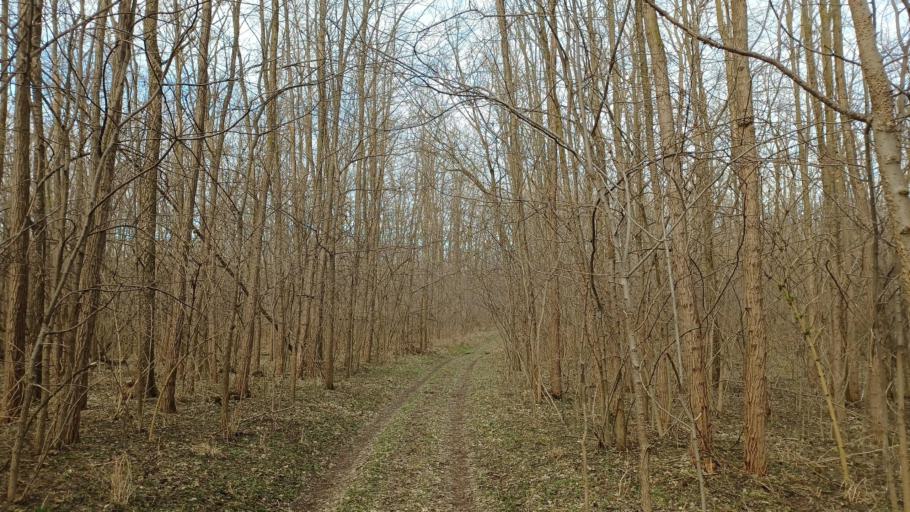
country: HU
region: Tolna
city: Tengelic
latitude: 46.5408
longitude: 18.6980
